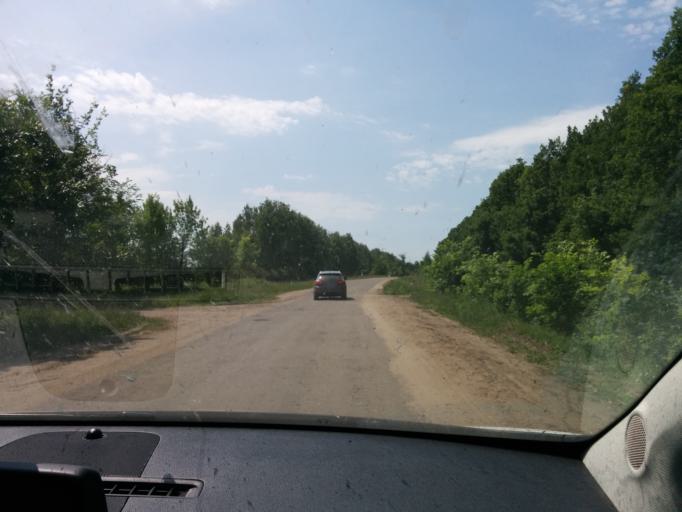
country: RU
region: Tambov
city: Morshansk
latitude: 53.6140
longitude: 41.8293
